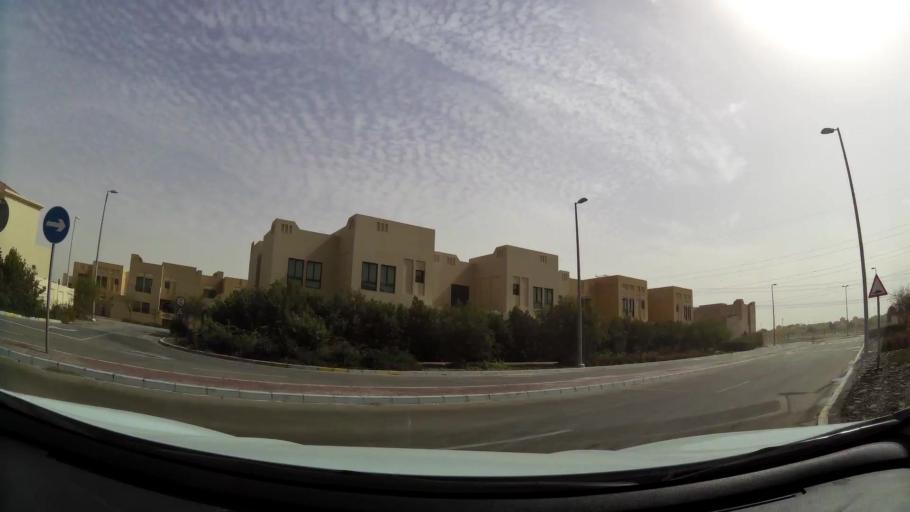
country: AE
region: Abu Dhabi
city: Abu Dhabi
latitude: 24.4071
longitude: 54.5331
